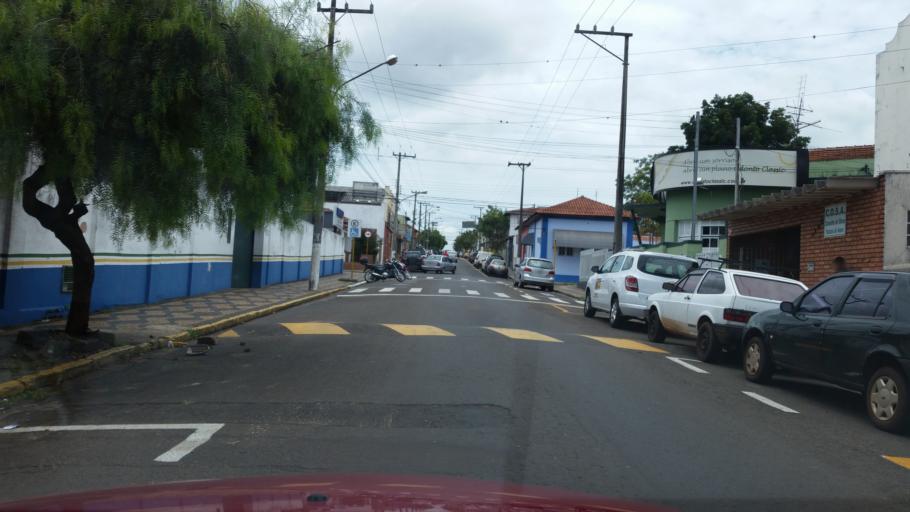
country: BR
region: Sao Paulo
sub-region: Avare
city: Avare
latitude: -23.0999
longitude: -48.9262
